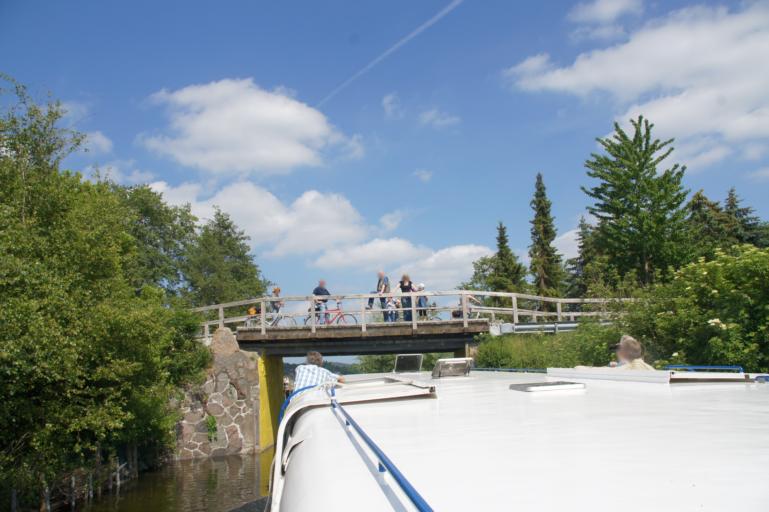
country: DE
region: Schleswig-Holstein
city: Bosdorf
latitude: 54.1680
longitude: 10.4950
